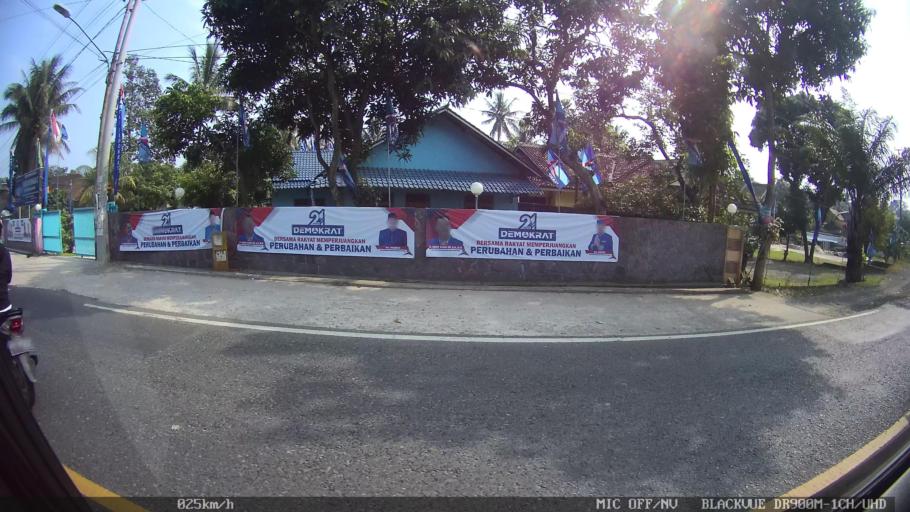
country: ID
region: Lampung
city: Natar
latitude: -5.3668
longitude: 105.1670
